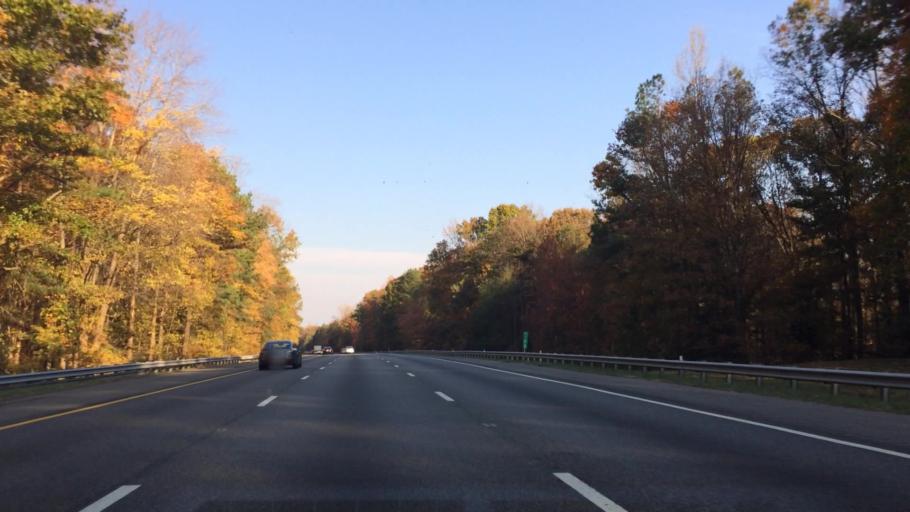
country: US
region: Virginia
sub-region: Caroline County
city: Bowling Green
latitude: 37.9540
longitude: -77.4815
